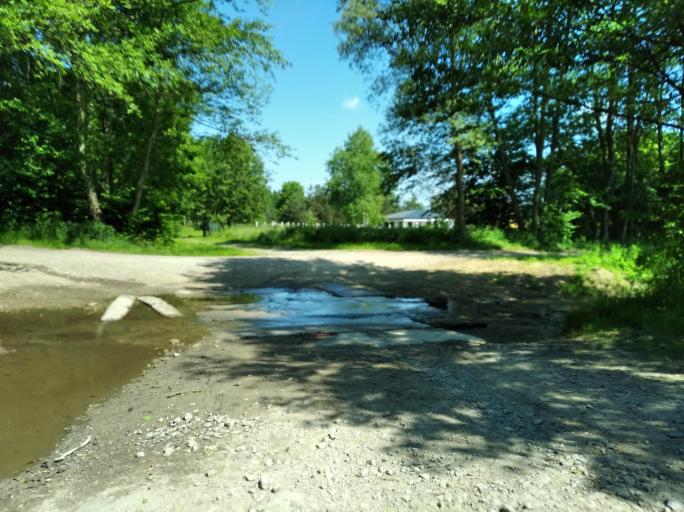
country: PL
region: Subcarpathian Voivodeship
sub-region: Powiat krosnienski
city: Odrzykon
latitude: 49.7784
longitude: 21.7611
